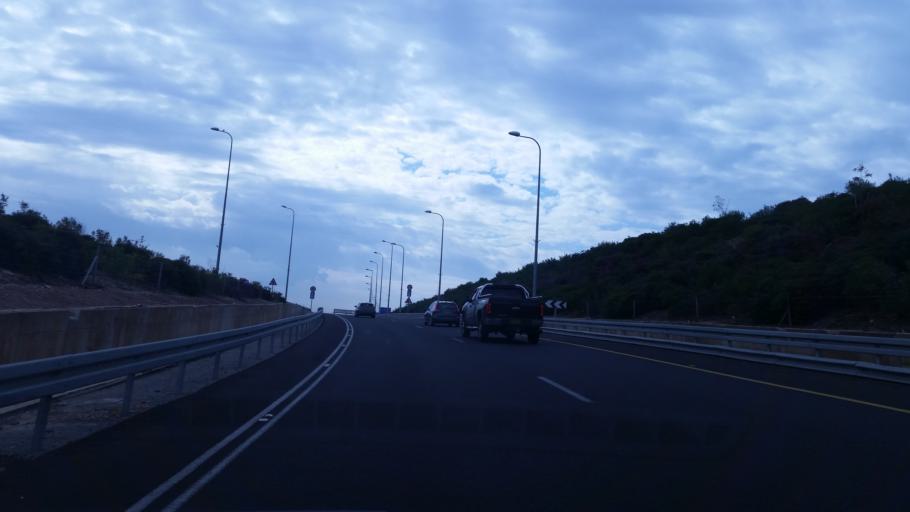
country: IL
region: Tel Aviv
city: Kefar Shemaryahu
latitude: 32.1922
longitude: 34.8295
